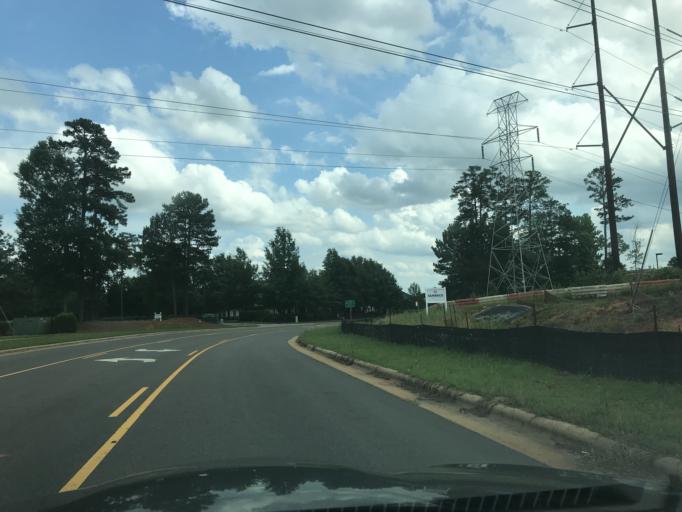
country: US
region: North Carolina
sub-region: Wake County
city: Wake Forest
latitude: 35.9102
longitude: -78.5912
